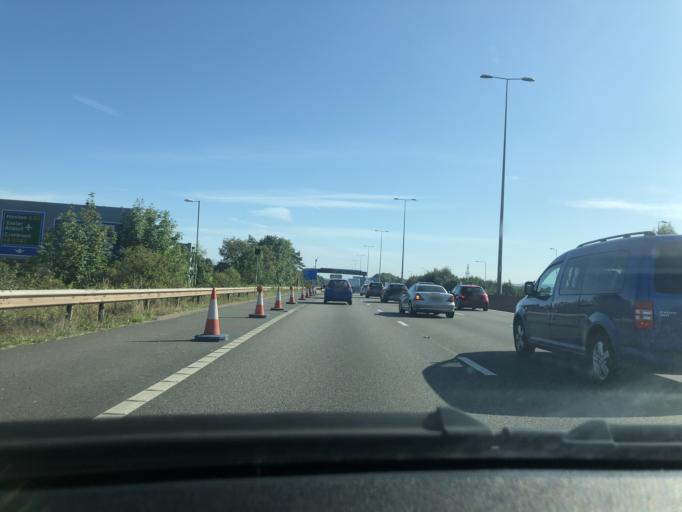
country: GB
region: England
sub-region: Devon
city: Heavitree
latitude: 50.7303
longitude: -3.4623
